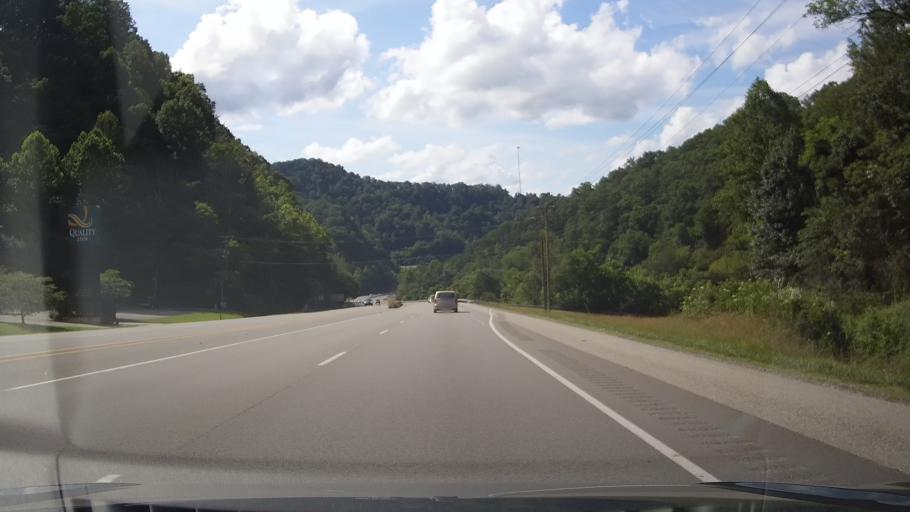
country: US
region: Kentucky
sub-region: Floyd County
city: Prestonsburg
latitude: 37.6455
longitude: -82.7778
